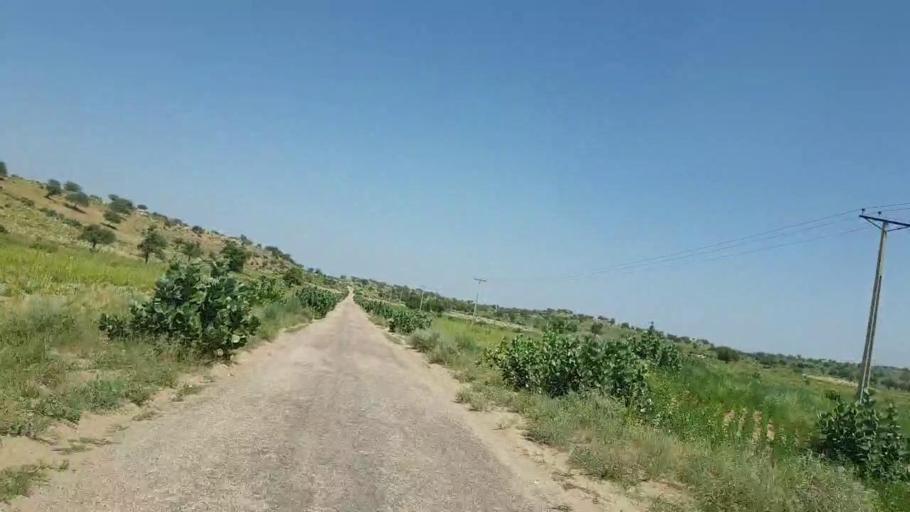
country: PK
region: Sindh
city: Islamkot
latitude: 25.1694
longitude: 70.4176
